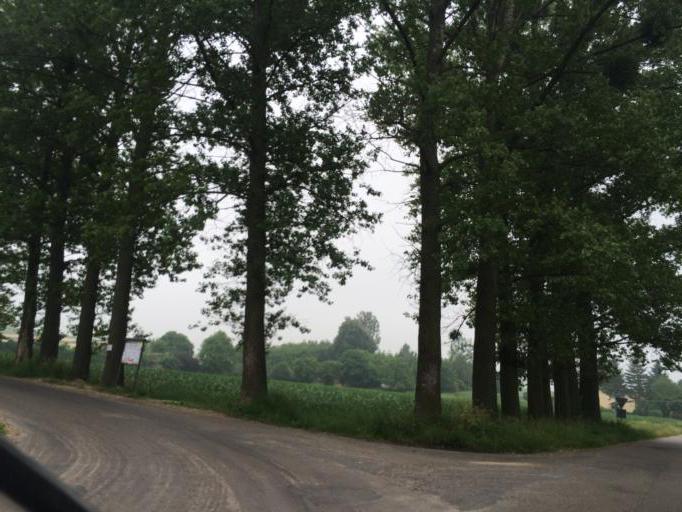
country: PL
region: Lublin Voivodeship
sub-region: Powiat pulawski
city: Markuszow
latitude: 51.3625
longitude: 22.2539
